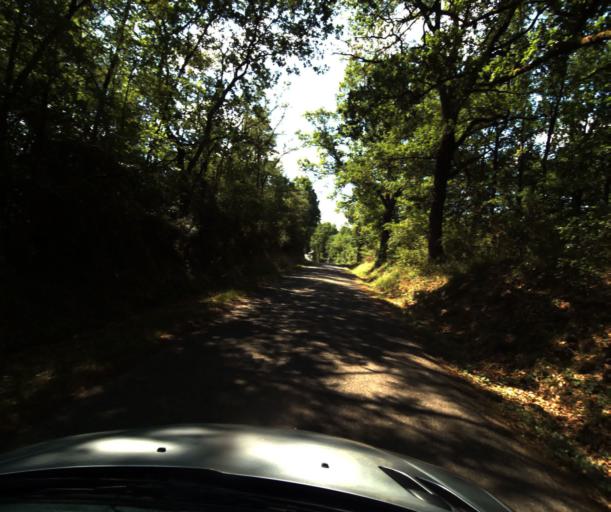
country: FR
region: Midi-Pyrenees
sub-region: Departement du Tarn-et-Garonne
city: Finhan
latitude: 43.8987
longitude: 1.2716
